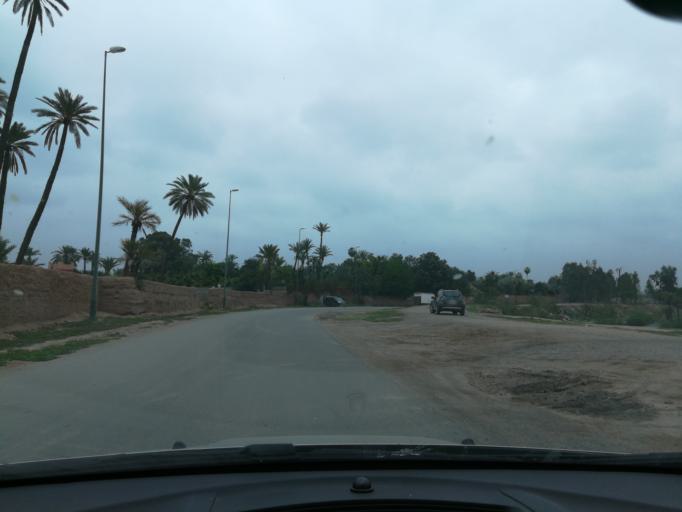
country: MA
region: Marrakech-Tensift-Al Haouz
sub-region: Marrakech
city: Marrakesh
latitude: 31.6611
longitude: -7.9831
